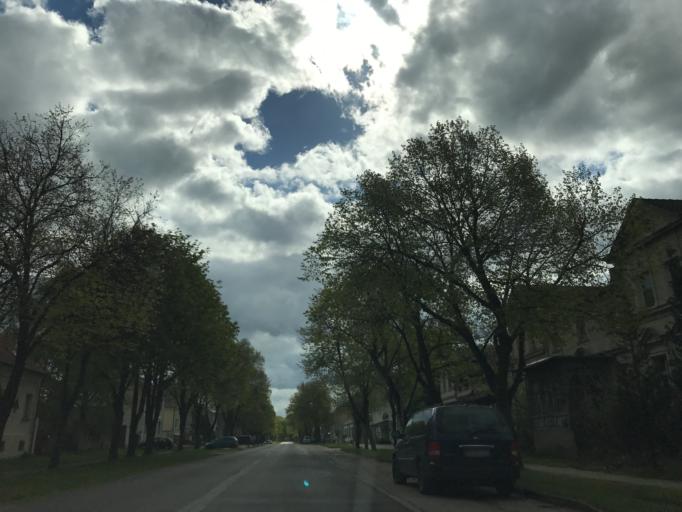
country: DE
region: Brandenburg
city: Roskow
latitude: 52.4729
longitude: 12.7134
